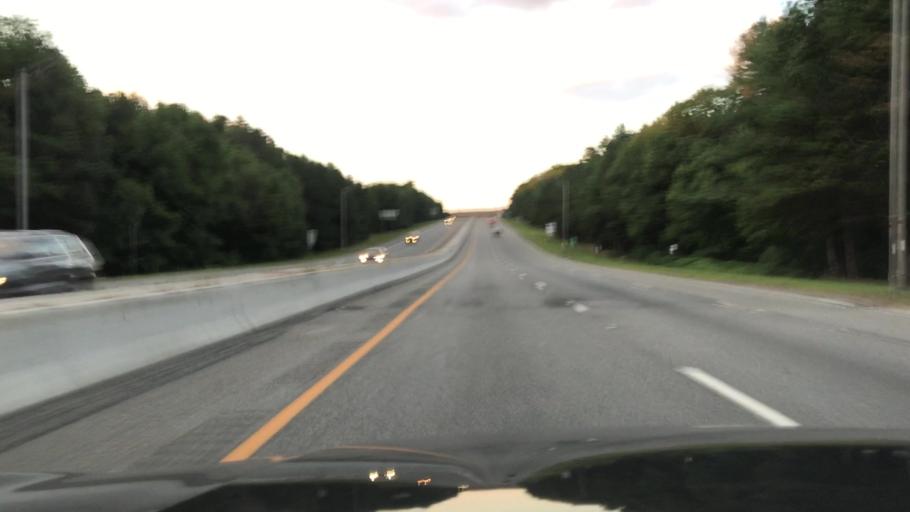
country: US
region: Rhode Island
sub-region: Washington County
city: Hope Valley
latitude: 41.5153
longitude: -71.6904
